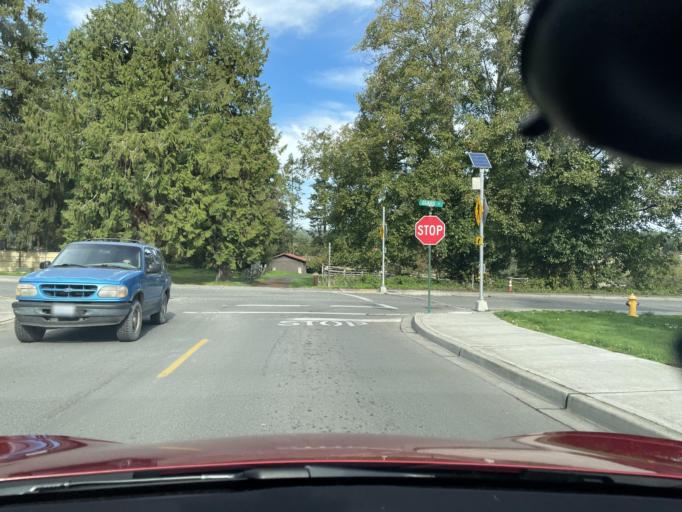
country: US
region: Washington
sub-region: San Juan County
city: Friday Harbor
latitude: 48.5360
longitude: -123.0269
